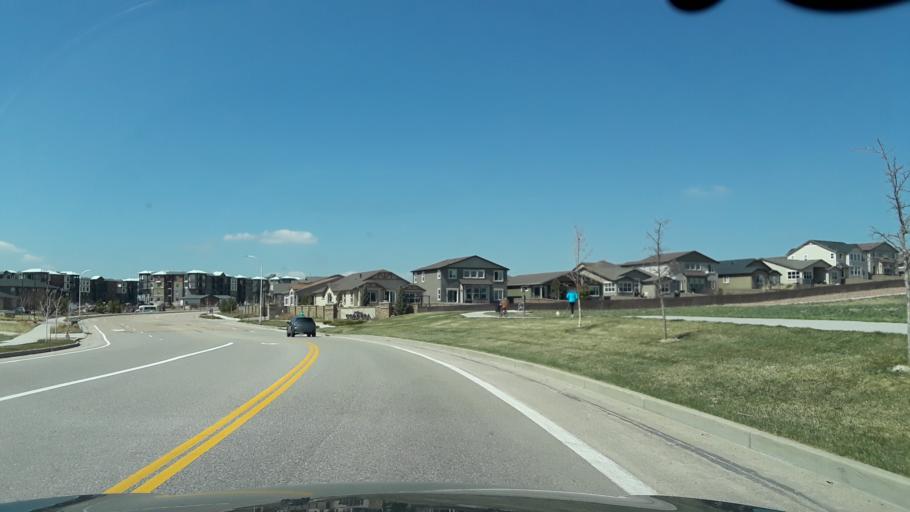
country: US
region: Colorado
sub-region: El Paso County
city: Black Forest
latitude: 38.9616
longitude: -104.7277
